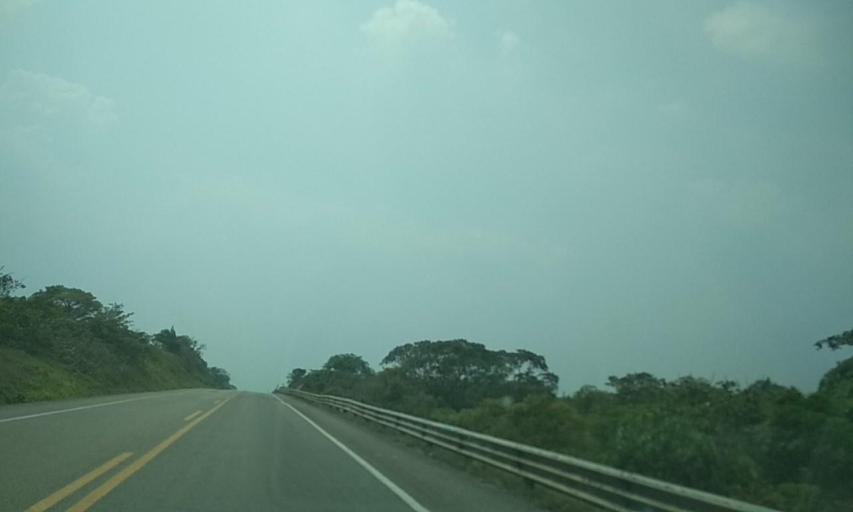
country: MX
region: Tabasco
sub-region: Huimanguillo
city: Francisco Rueda
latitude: 17.7403
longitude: -93.9810
